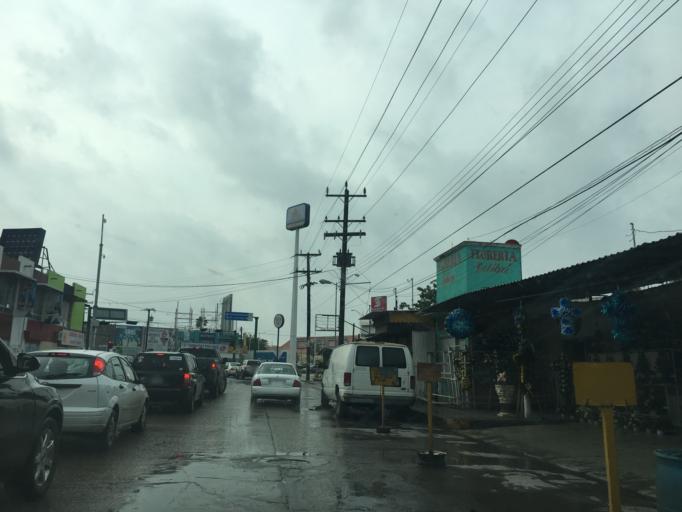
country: MX
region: Tamaulipas
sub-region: Matamoros
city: Heroica Matamoros
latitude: 25.8712
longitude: -97.5047
